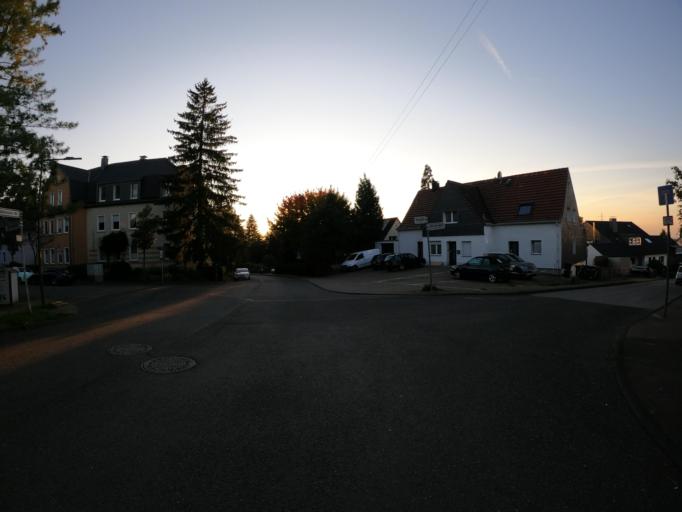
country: DE
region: North Rhine-Westphalia
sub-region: Regierungsbezirk Dusseldorf
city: Wuppertal
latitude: 51.2278
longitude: 7.1297
